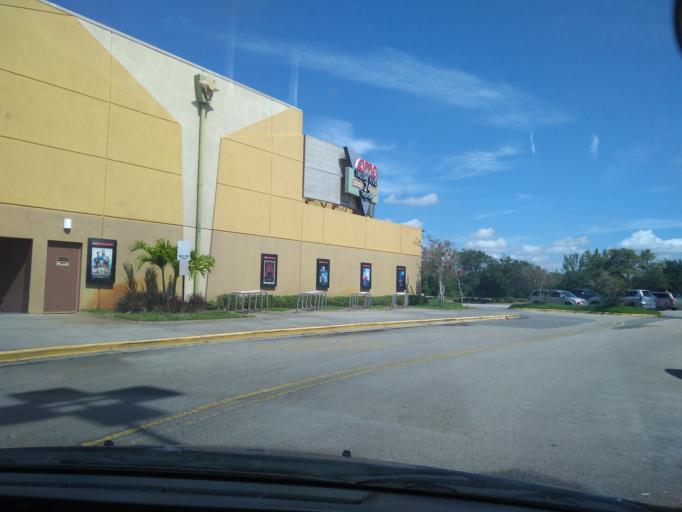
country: US
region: Florida
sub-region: Indian River County
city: West Vero Corridor
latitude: 27.6435
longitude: -80.4588
